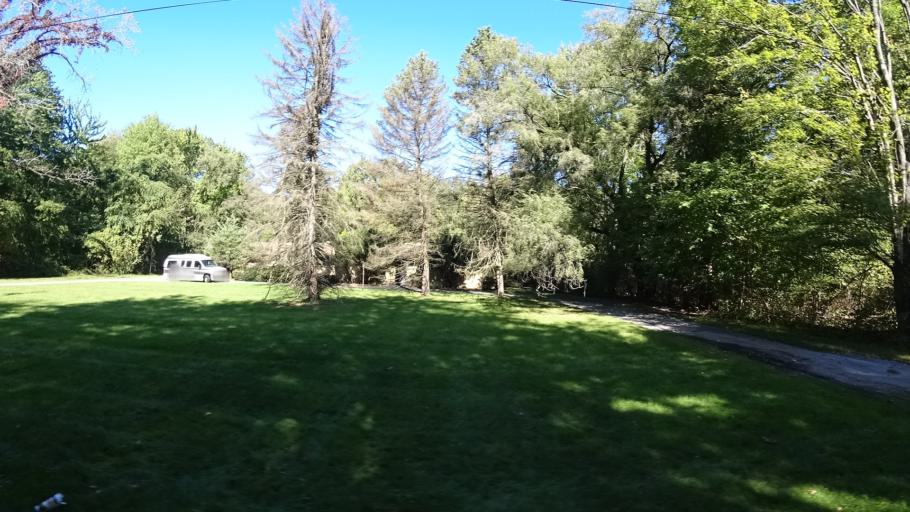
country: US
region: Indiana
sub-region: LaPorte County
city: Trail Creek
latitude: 41.6875
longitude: -86.8770
